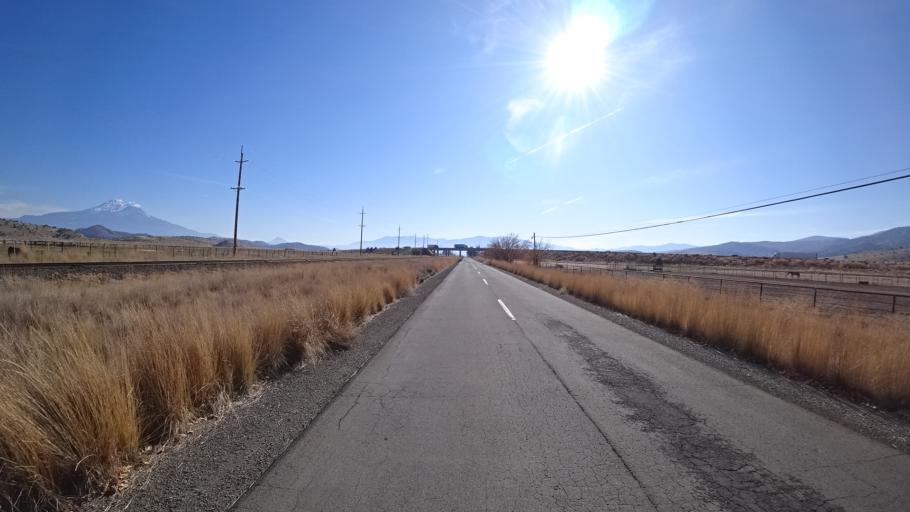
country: US
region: California
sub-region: Siskiyou County
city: Montague
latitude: 41.6313
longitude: -122.5219
